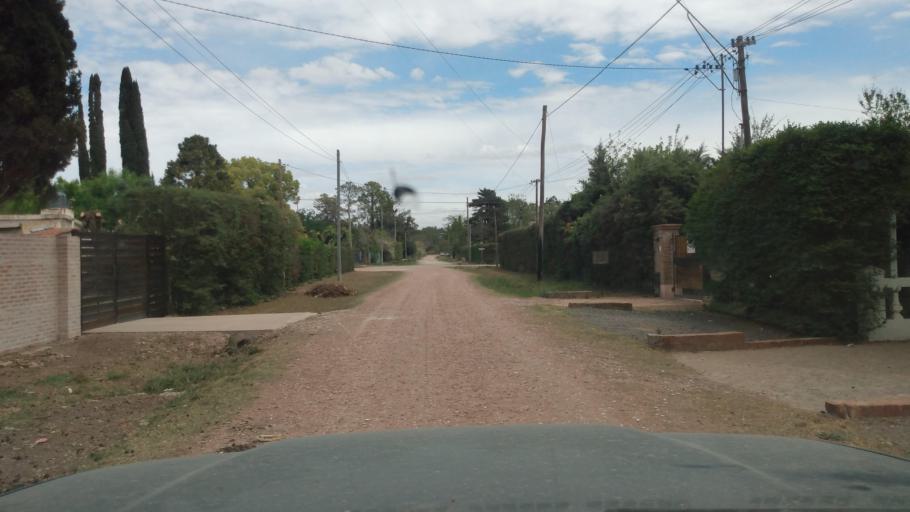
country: AR
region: Buenos Aires
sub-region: Partido de Lujan
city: Lujan
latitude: -34.5897
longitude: -59.1310
